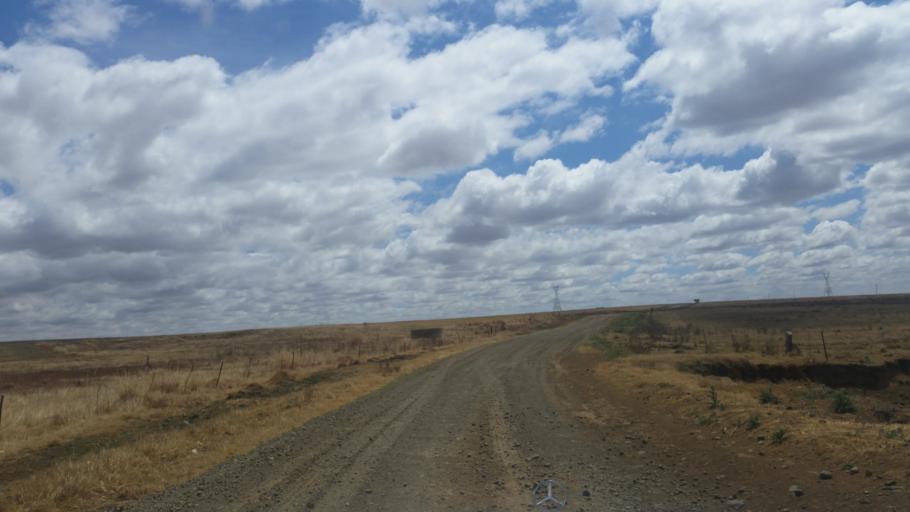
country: ZA
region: Orange Free State
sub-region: Thabo Mofutsanyana District Municipality
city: Harrismith
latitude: -28.2484
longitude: 28.9298
